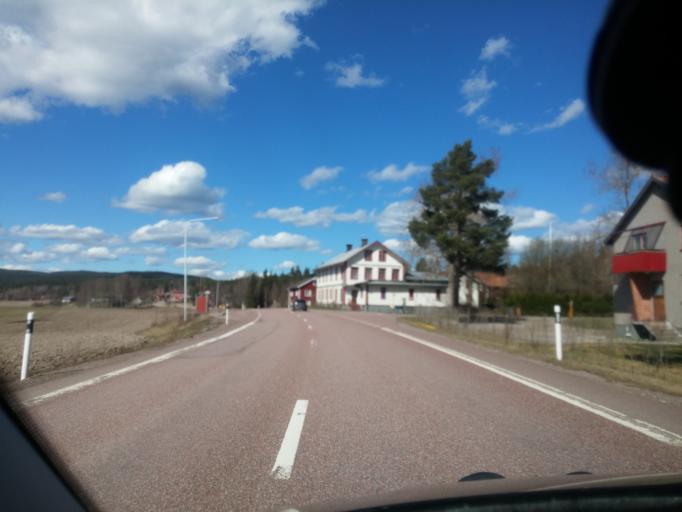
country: SE
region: Dalarna
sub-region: Faluns Kommun
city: Svardsjo
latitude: 60.7177
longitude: 15.7792
